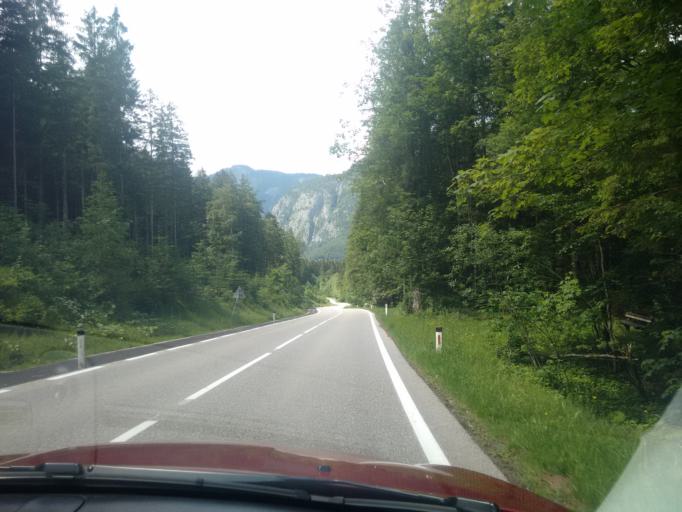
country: AT
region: Styria
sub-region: Politischer Bezirk Liezen
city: Bad Aussee
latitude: 47.5474
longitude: 13.7025
